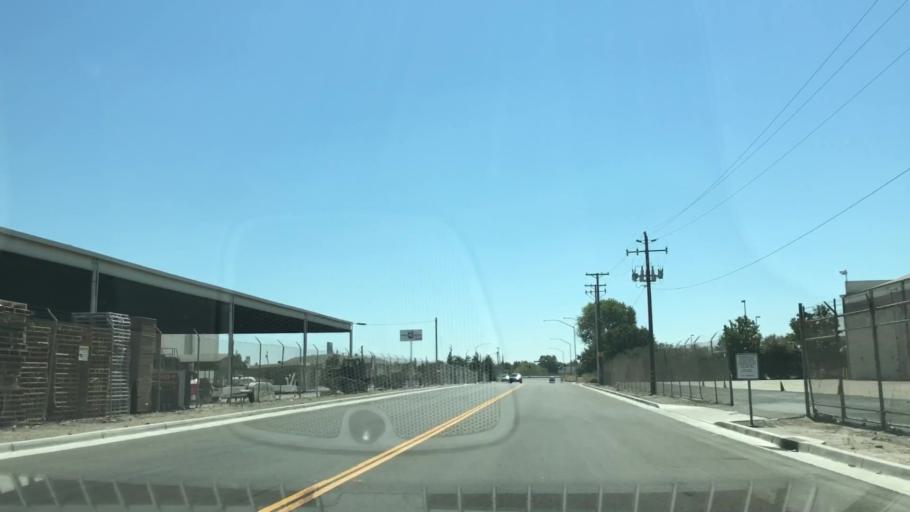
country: US
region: California
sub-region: San Joaquin County
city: Stockton
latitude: 37.9339
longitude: -121.3183
